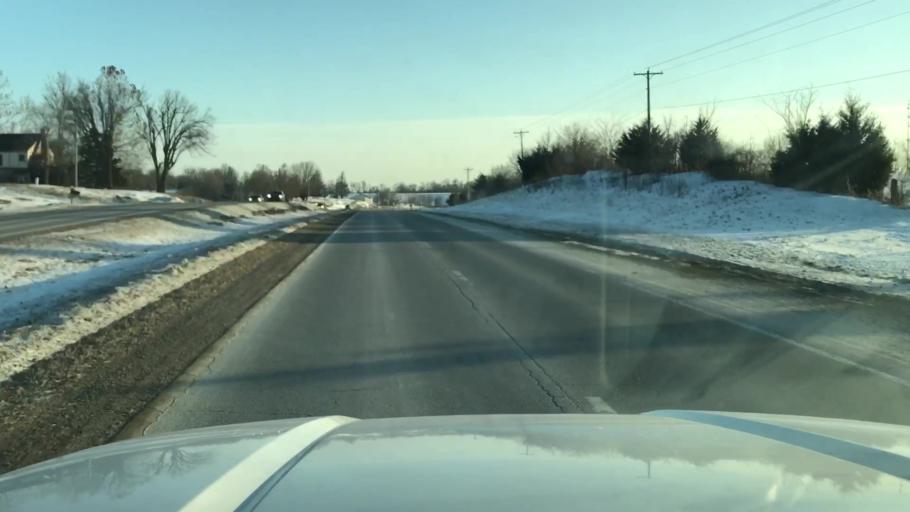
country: US
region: Missouri
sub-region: Andrew County
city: Country Club Village
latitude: 39.8703
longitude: -94.8086
